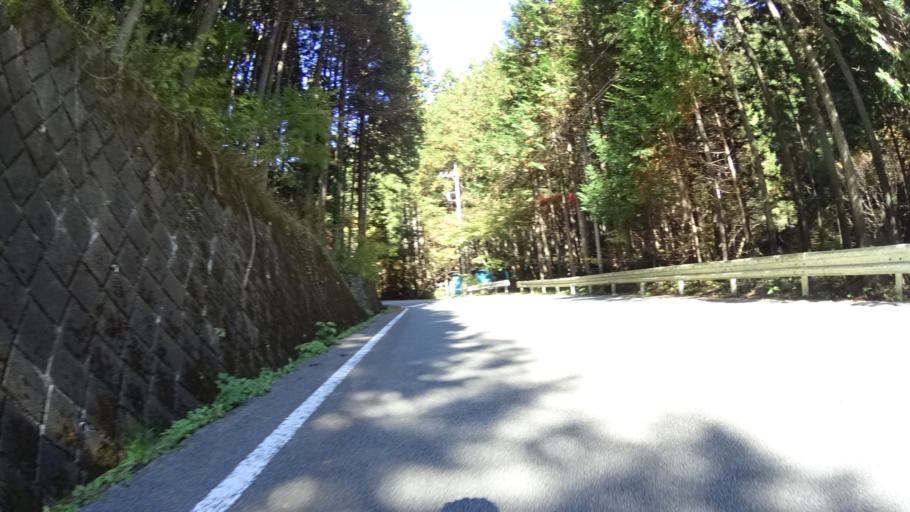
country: JP
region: Yamanashi
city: Otsuki
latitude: 35.7641
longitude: 138.9372
